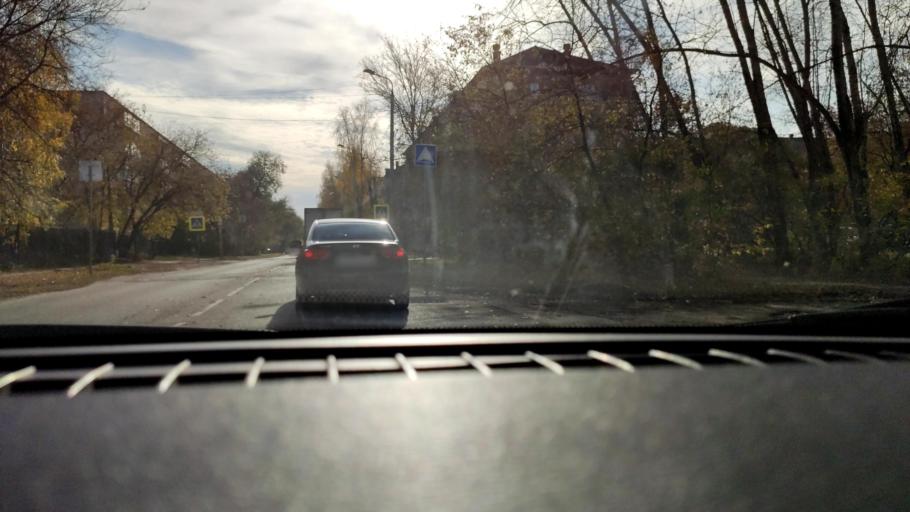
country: RU
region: Perm
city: Overyata
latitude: 58.0191
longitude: 55.9763
